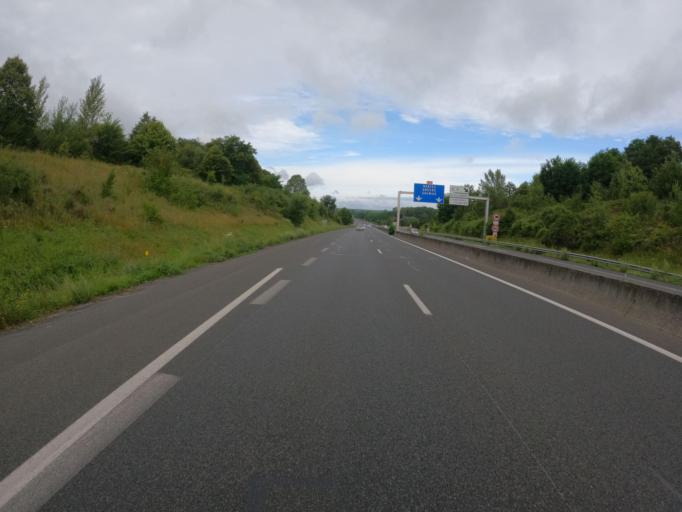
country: FR
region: Centre
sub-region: Departement d'Indre-et-Loire
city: Cinq-Mars-la-Pile
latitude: 47.3254
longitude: 0.4794
